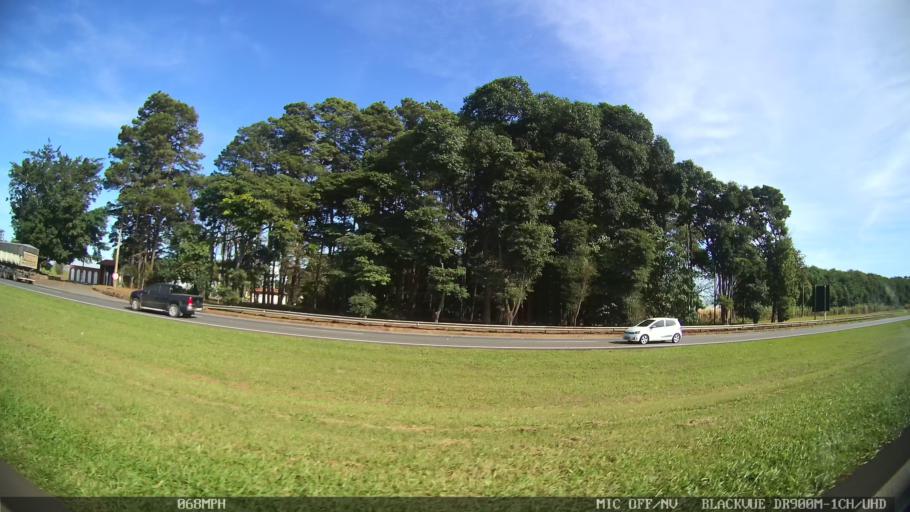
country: BR
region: Sao Paulo
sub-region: Cordeiropolis
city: Cordeiropolis
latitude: -22.4617
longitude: -47.3989
